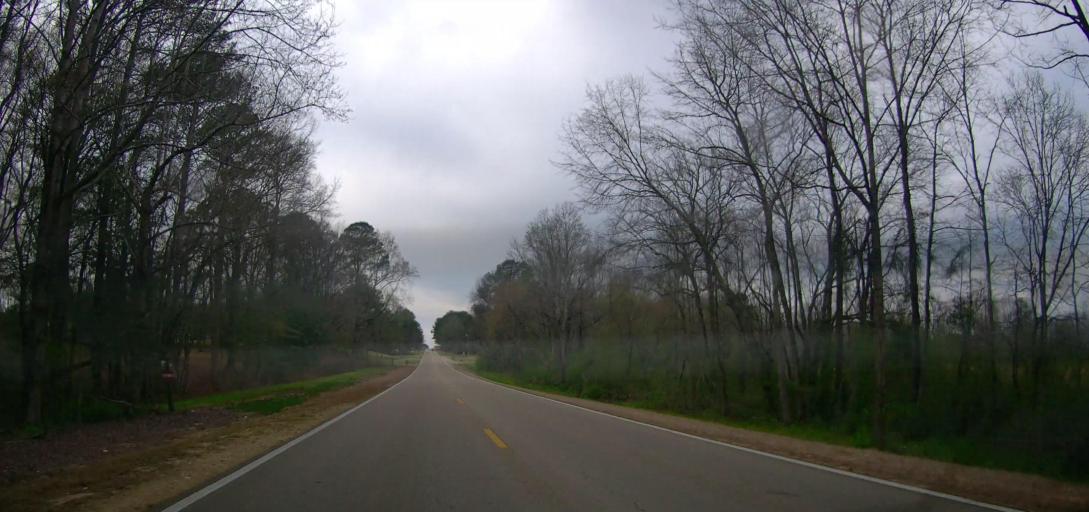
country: US
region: Mississippi
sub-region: Itawamba County
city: Mantachie
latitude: 34.2533
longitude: -88.4805
